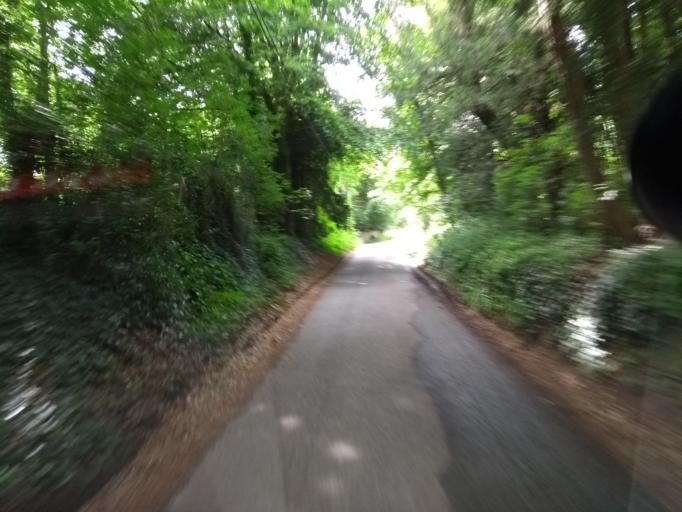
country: GB
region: England
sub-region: Somerset
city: Ilminster
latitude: 50.9353
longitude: -2.8854
